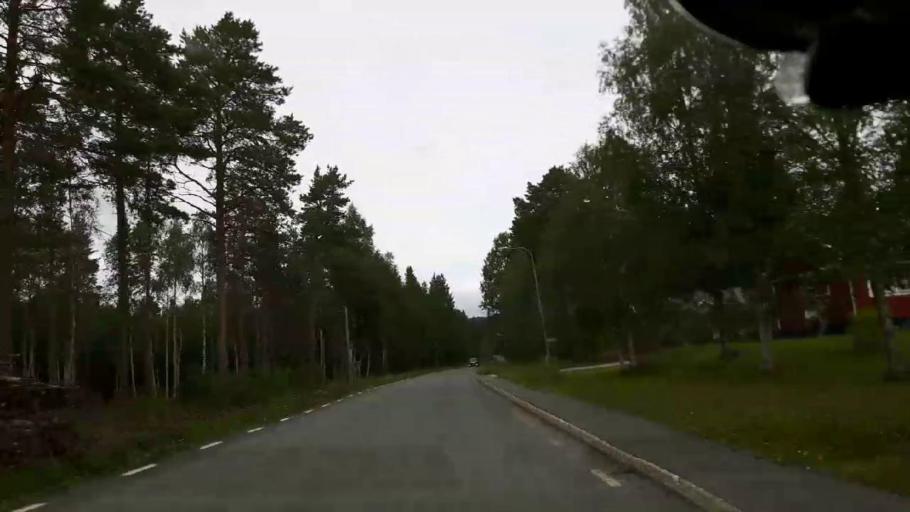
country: SE
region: Jaemtland
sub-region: Krokoms Kommun
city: Valla
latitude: 63.4608
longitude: 14.0621
